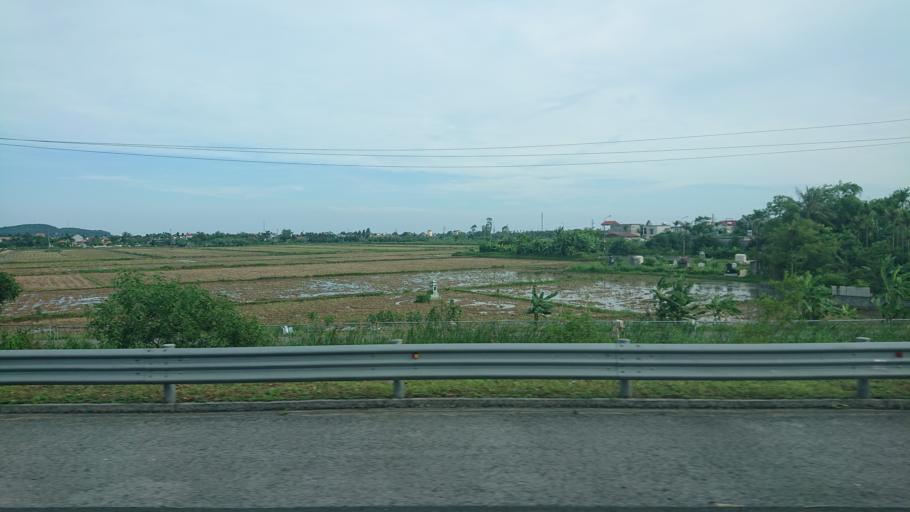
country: VN
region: Hai Phong
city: Nui Doi
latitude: 20.7660
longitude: 106.6475
